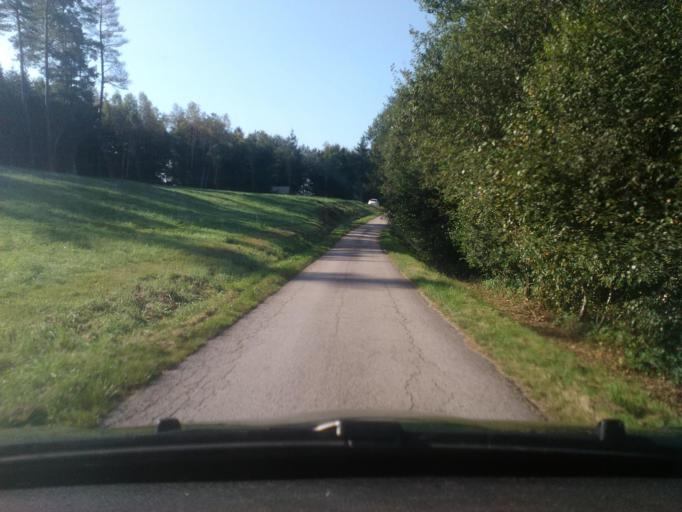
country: FR
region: Lorraine
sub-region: Departement des Vosges
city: Moyenmoutier
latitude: 48.3657
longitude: 6.9101
